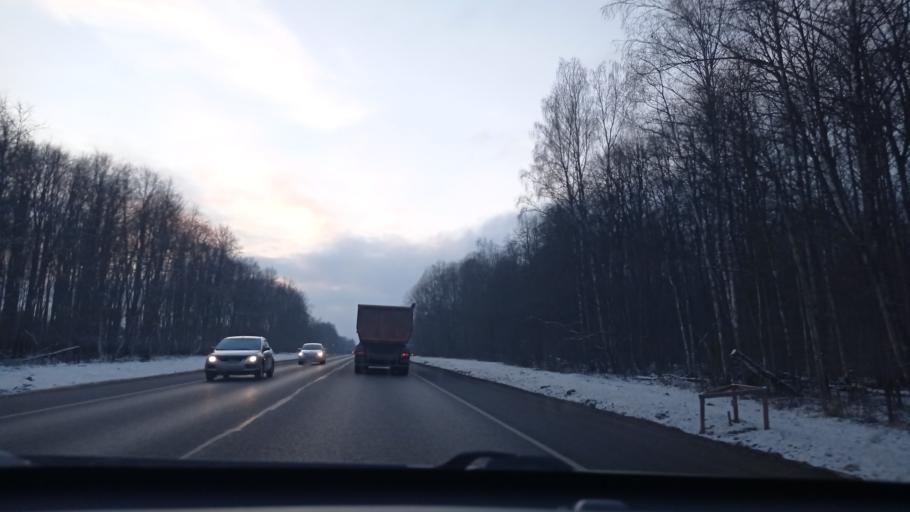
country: RU
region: Kaluga
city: Zhukovo
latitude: 55.1644
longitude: 36.8499
